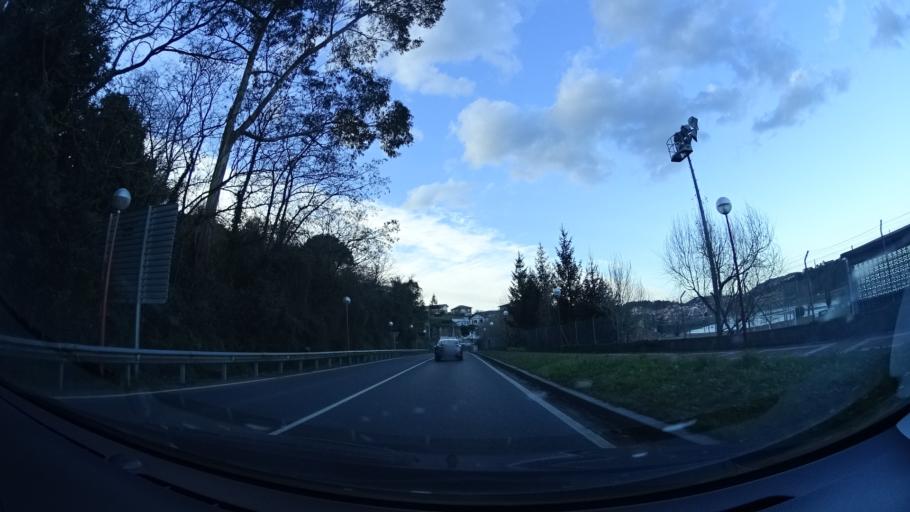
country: ES
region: Basque Country
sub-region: Bizkaia
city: Plentzia
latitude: 43.3970
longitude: -2.9453
